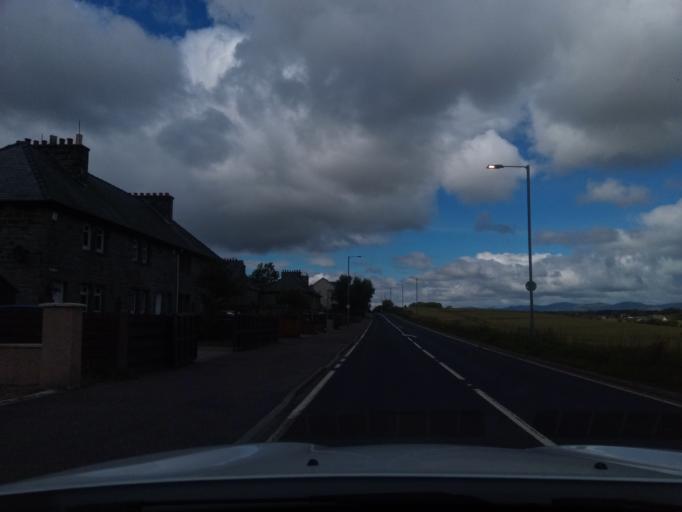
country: GB
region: Scotland
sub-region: Fife
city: Cairneyhill
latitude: 56.0494
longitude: -3.5280
